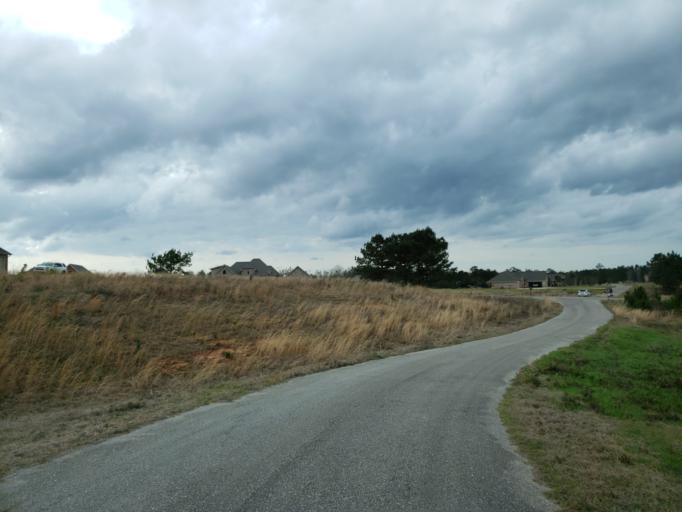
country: US
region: Mississippi
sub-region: Jones County
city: Ellisville
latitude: 31.5529
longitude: -89.2538
